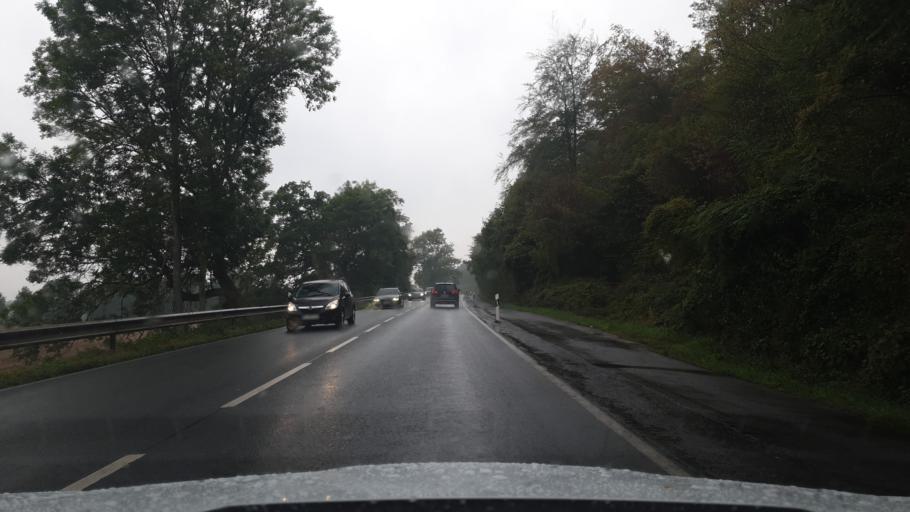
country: DE
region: North Rhine-Westphalia
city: Porta Westfalica
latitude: 52.2414
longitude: 8.9003
